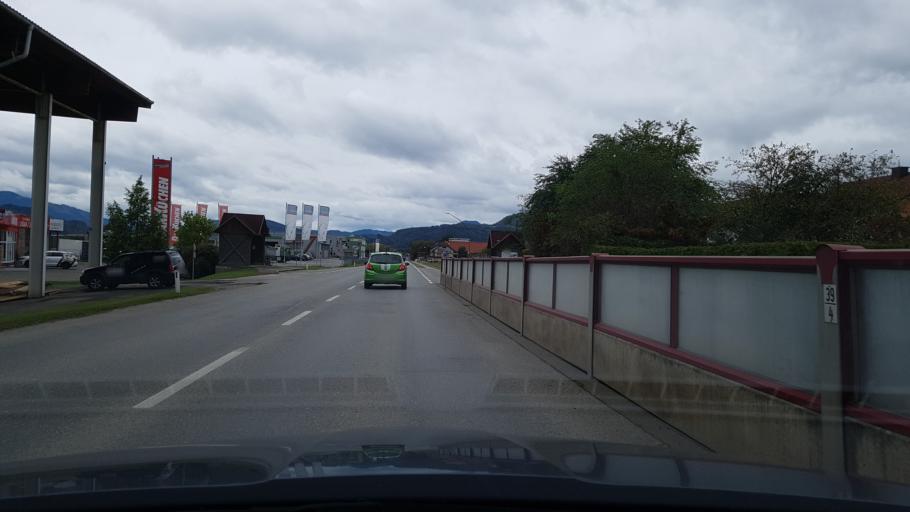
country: AT
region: Styria
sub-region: Politischer Bezirk Bruck-Muerzzuschlag
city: Sankt Marein im Muerztal
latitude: 47.4723
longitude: 15.3619
